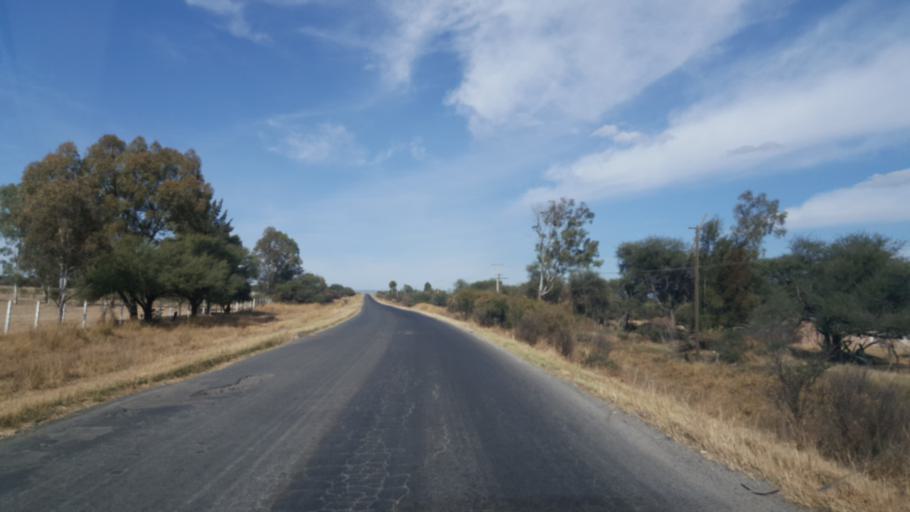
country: MX
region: Jalisco
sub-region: Lagos de Moreno
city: Geovillas Laureles del Campanario
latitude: 21.2962
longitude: -101.9289
